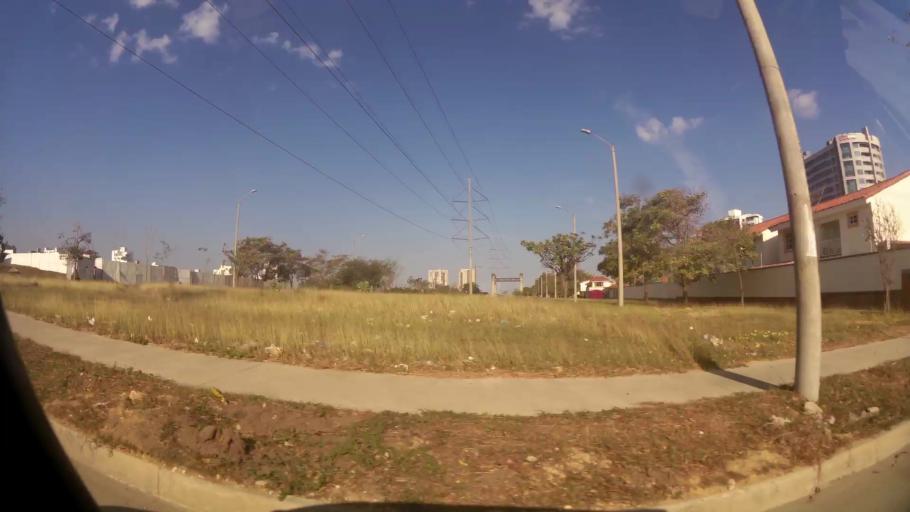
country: CO
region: Atlantico
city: Barranquilla
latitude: 11.0142
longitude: -74.8311
